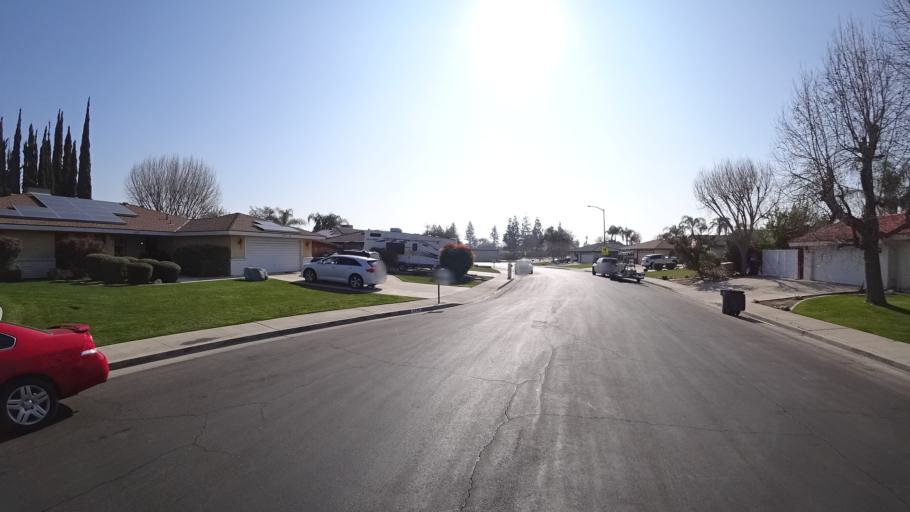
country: US
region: California
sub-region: Kern County
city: Bakersfield
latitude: 35.3309
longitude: -119.0673
